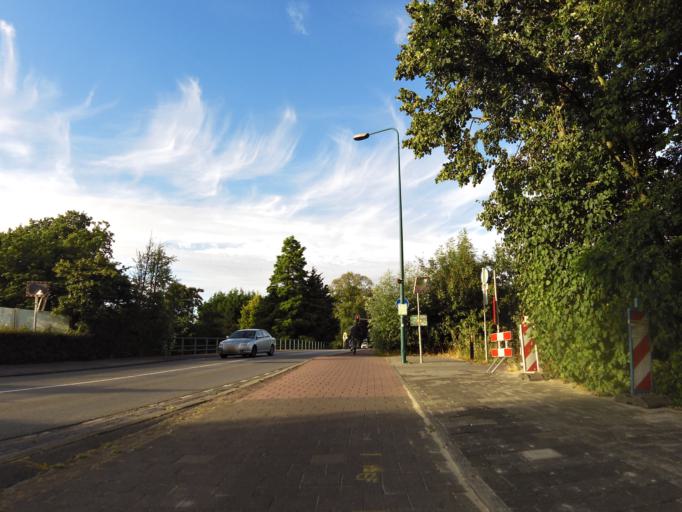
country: NL
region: South Holland
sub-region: Gemeente Oegstgeest
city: Oegstgeest
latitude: 52.1868
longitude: 4.4889
